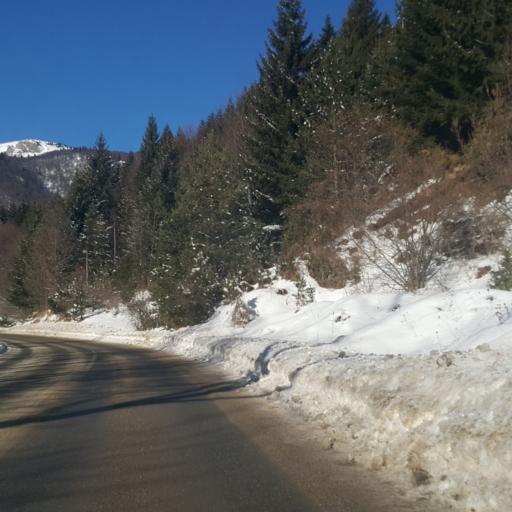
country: XK
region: Mitrovica
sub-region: Komuna e Leposaviqit
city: Leposaviq
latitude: 43.3062
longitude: 20.8699
